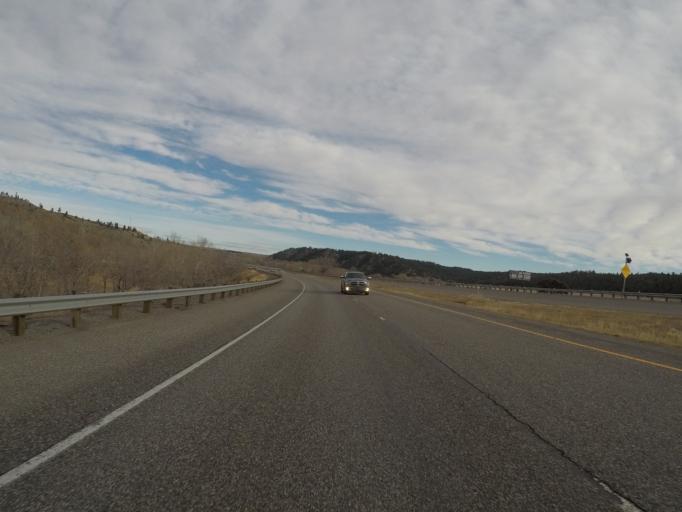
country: US
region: Montana
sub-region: Stillwater County
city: Absarokee
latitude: 45.6815
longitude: -109.4352
